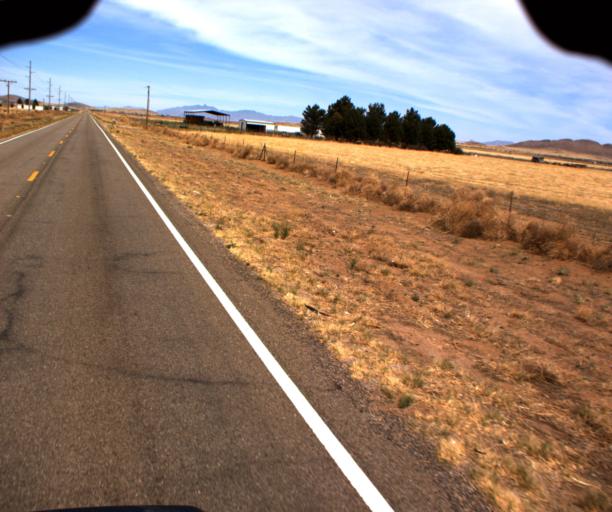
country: US
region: Arizona
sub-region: Cochise County
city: Tombstone
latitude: 31.8342
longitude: -109.6952
